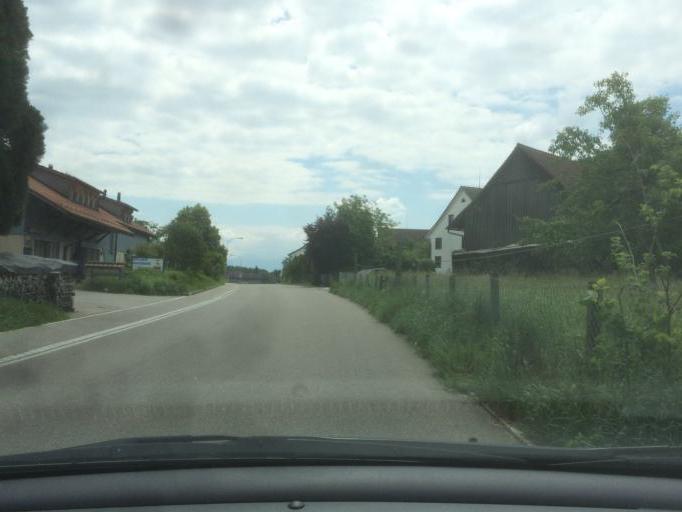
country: CH
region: Zurich
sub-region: Bezirk Hinwil
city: Wetzikon / Robenhausen
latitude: 47.3453
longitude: 8.7677
